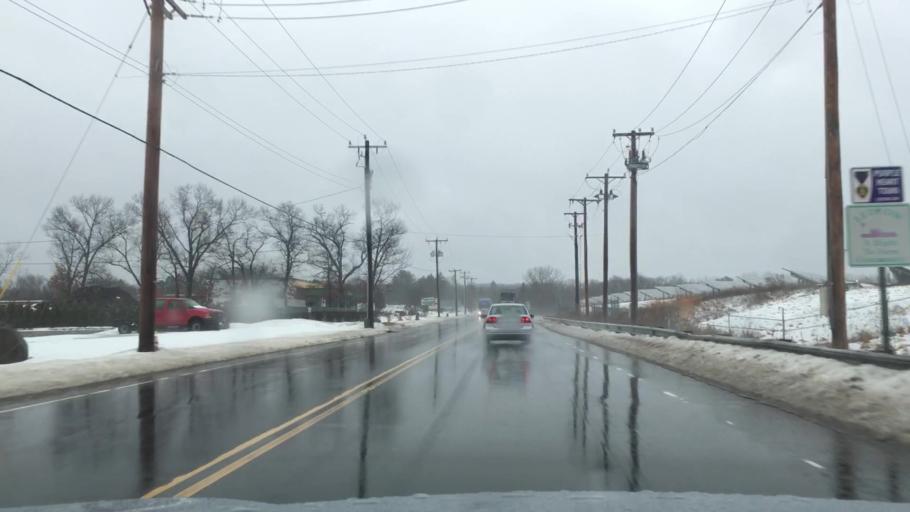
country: US
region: Massachusetts
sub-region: Hampden County
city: Ludlow
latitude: 42.1809
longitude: -72.5140
